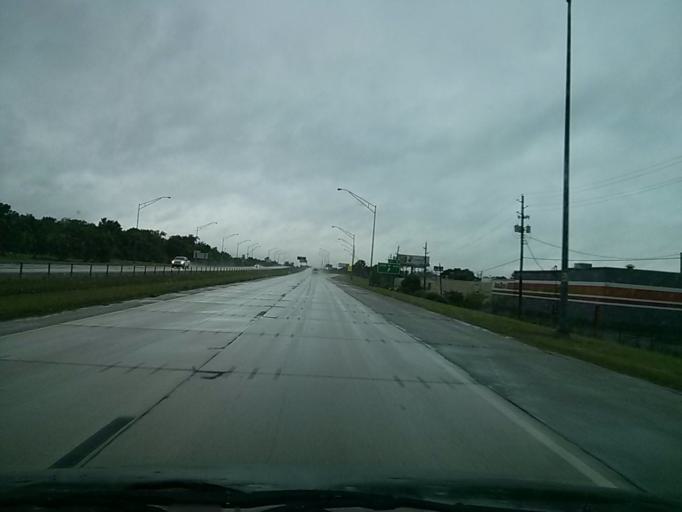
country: US
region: Oklahoma
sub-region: Tulsa County
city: Oakhurst
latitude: 36.1014
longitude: -96.0254
